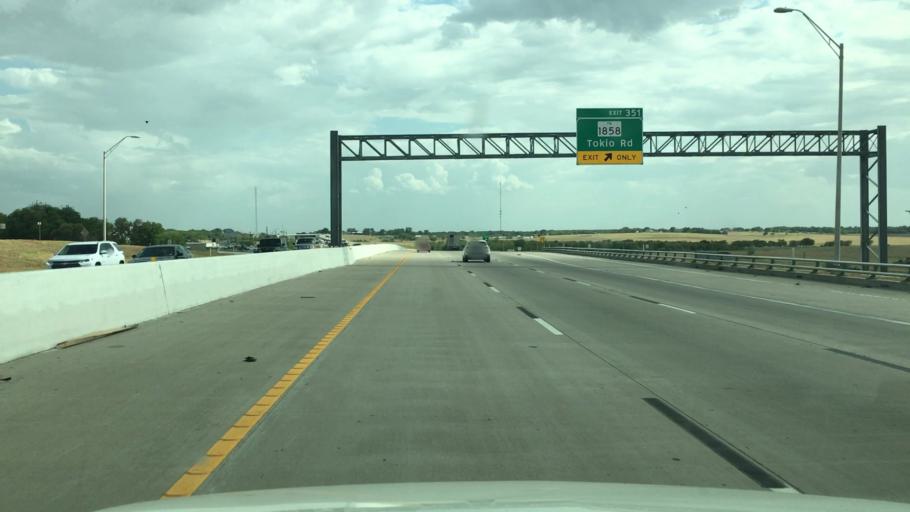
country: US
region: Texas
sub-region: McLennan County
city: West
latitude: 31.8027
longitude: -97.1001
